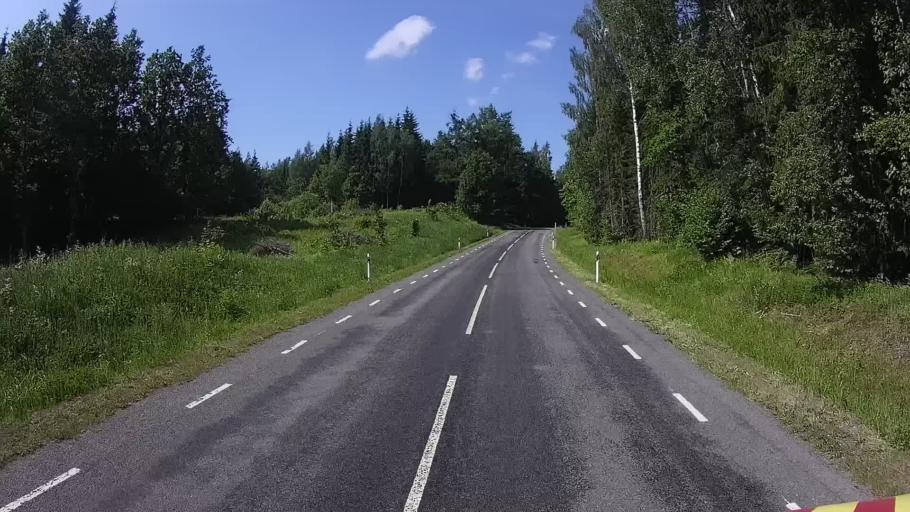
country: EE
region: Viljandimaa
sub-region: Karksi vald
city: Karksi-Nuia
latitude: 58.0829
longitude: 25.5586
